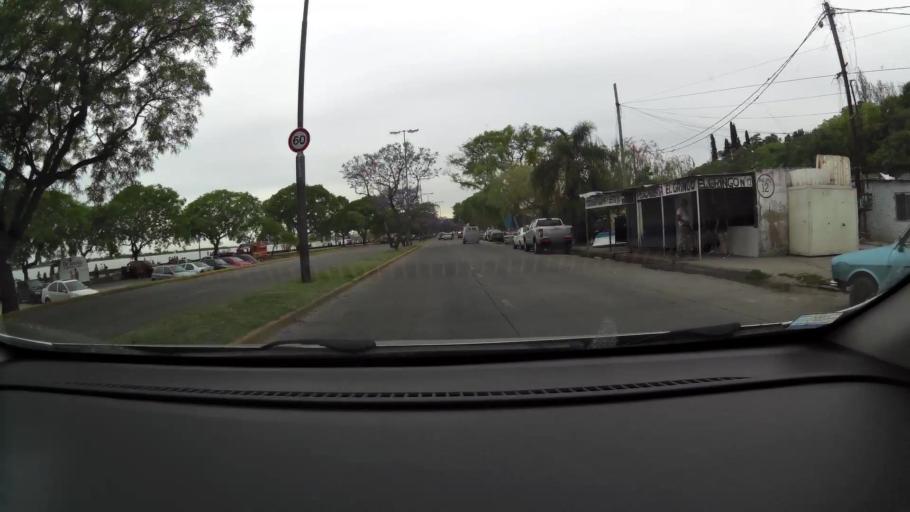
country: AR
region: Santa Fe
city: Granadero Baigorria
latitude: -32.8855
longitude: -60.6878
